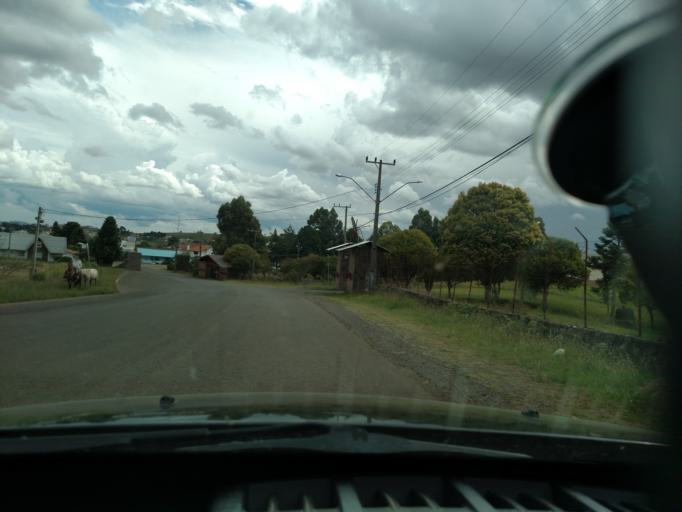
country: BR
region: Santa Catarina
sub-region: Sao Joaquim
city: Sao Joaquim
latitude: -28.2753
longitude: -49.9275
